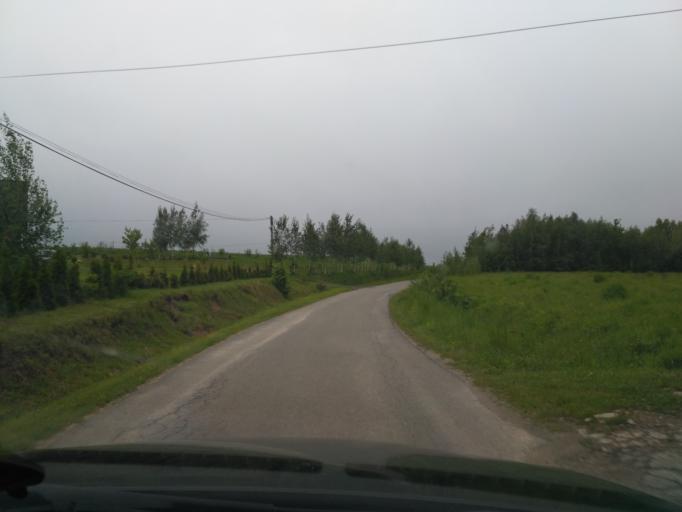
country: PL
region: Subcarpathian Voivodeship
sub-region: Powiat debicki
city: Jodlowa
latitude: 49.8553
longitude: 21.2529
